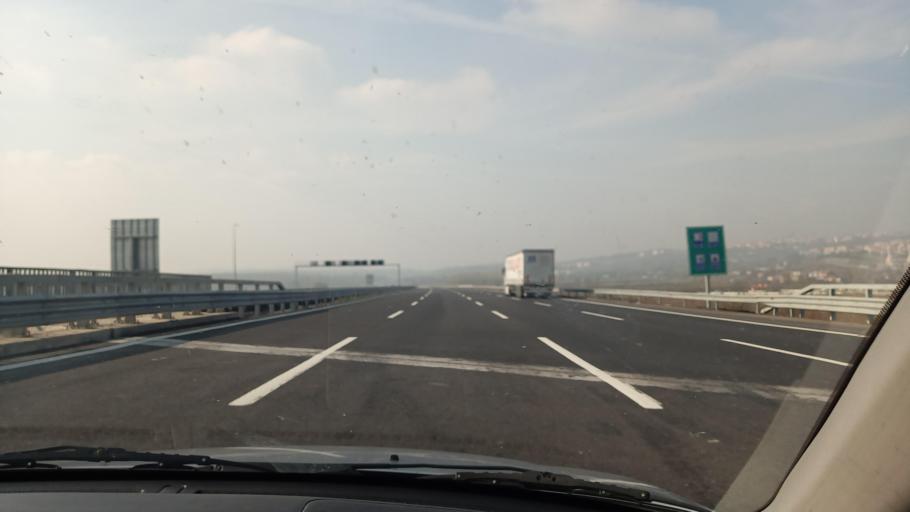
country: TR
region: Sakarya
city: Kazimpasa
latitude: 40.8444
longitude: 30.3284
